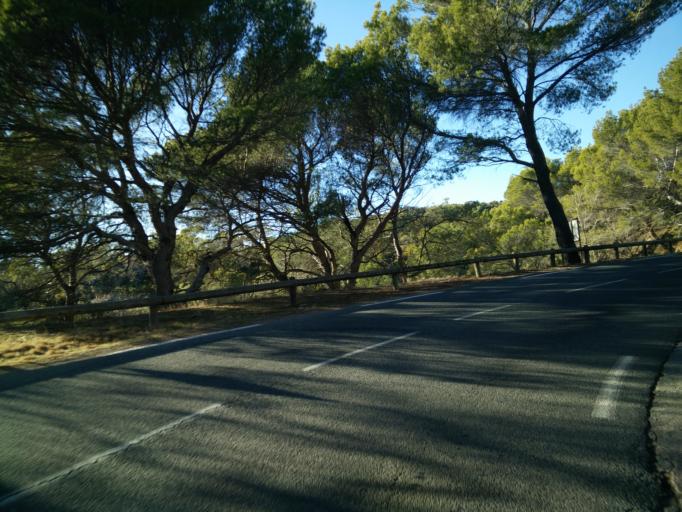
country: FR
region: Provence-Alpes-Cote d'Azur
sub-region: Departement du Var
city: Villecroze
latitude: 43.5835
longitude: 6.2698
